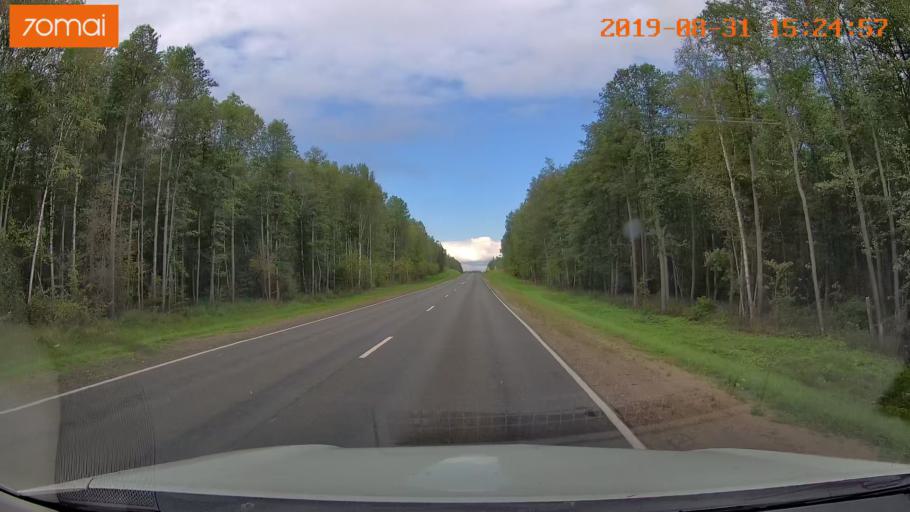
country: RU
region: Kaluga
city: Baryatino
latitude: 54.5348
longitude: 34.5124
